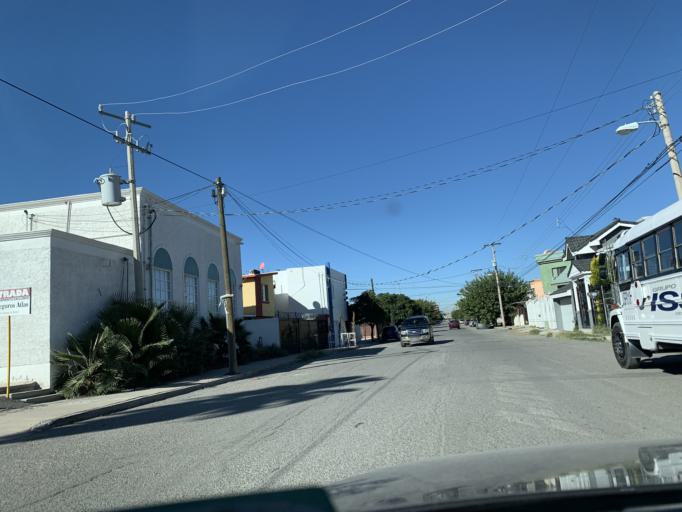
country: MX
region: Chihuahua
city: Ciudad Juarez
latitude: 31.7391
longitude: -106.4429
